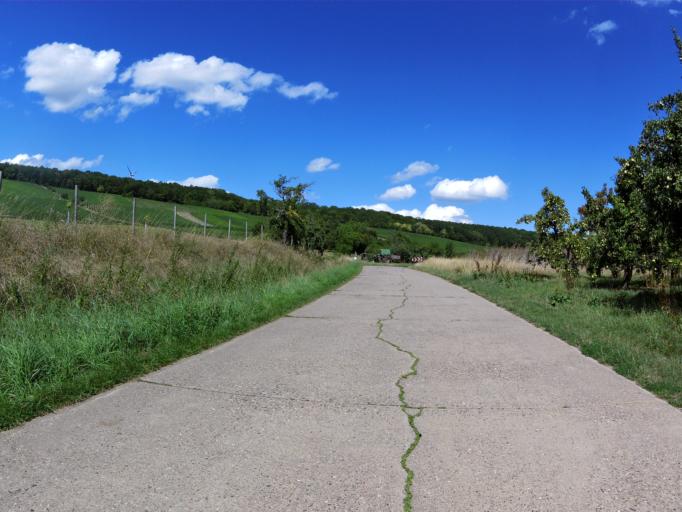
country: DE
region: Bavaria
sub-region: Regierungsbezirk Unterfranken
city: Wipfeld
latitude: 49.8870
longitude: 10.1602
